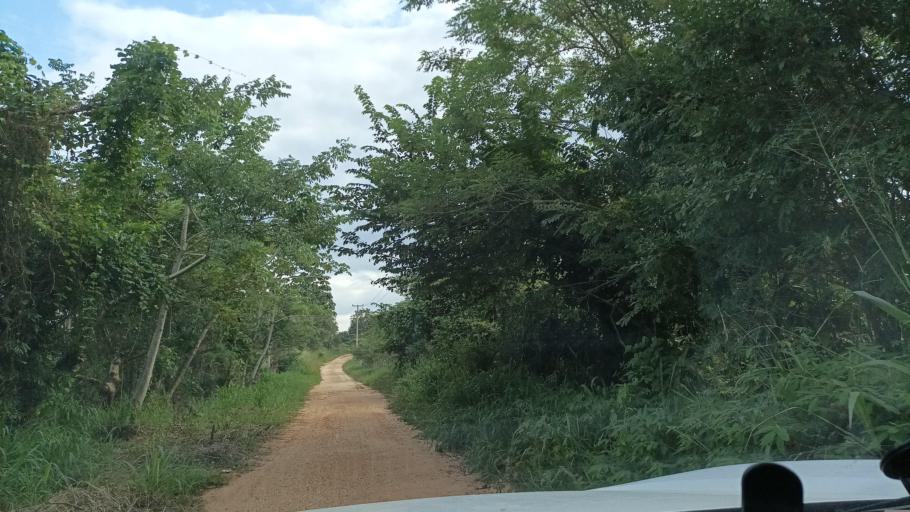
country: MX
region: Veracruz
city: Oluta
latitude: 17.9399
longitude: -94.8822
